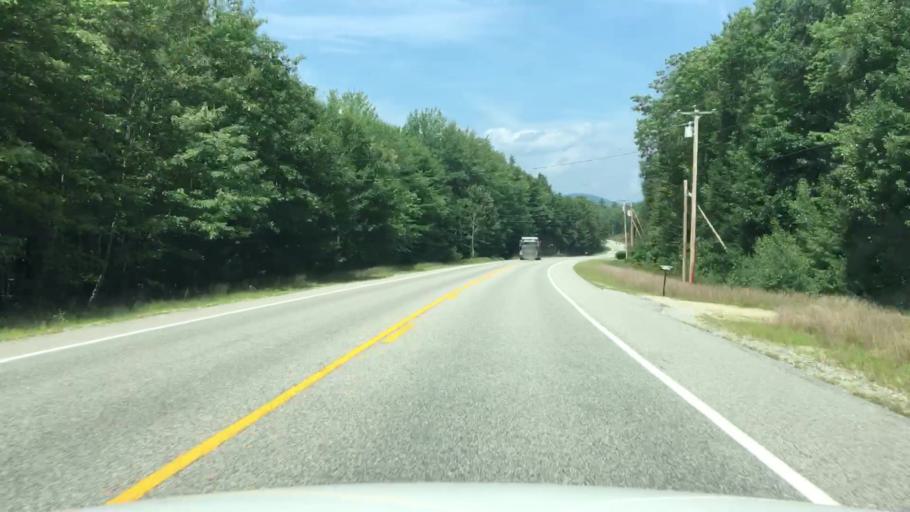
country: US
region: Maine
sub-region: Oxford County
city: Canton
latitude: 44.4734
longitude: -70.3264
